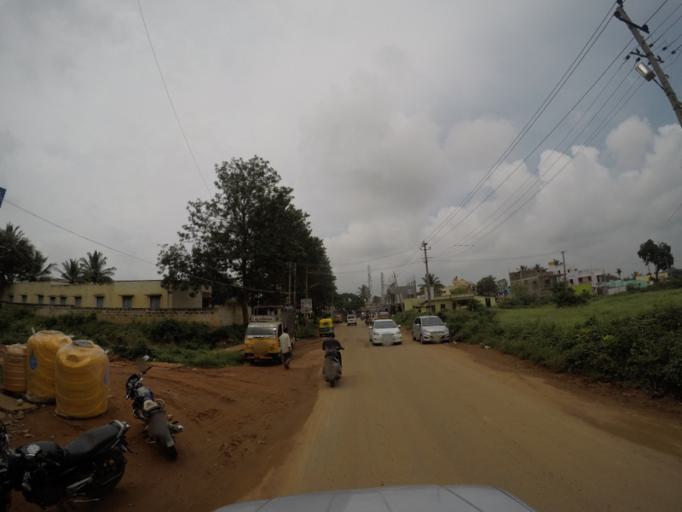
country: IN
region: Karnataka
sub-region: Bangalore Urban
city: Yelahanka
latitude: 13.1113
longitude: 77.5265
